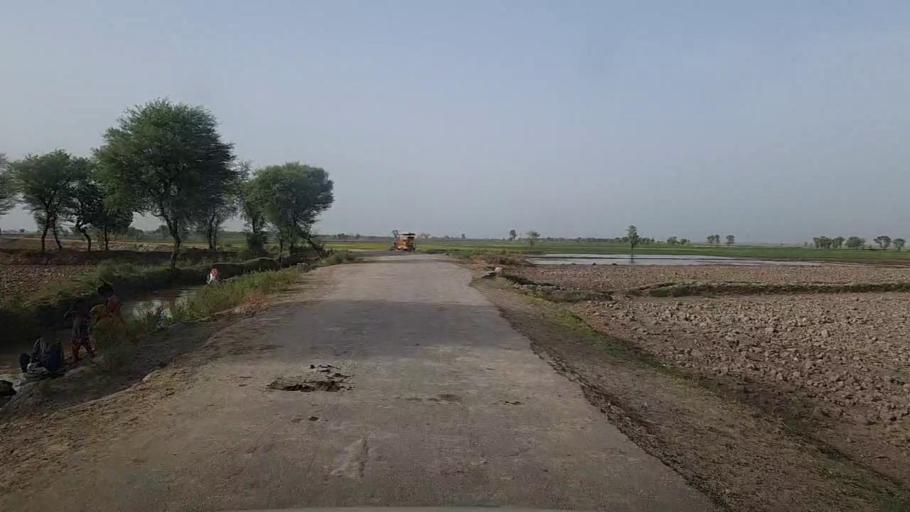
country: PK
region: Sindh
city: Khairpur Nathan Shah
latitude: 27.1000
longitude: 67.7922
